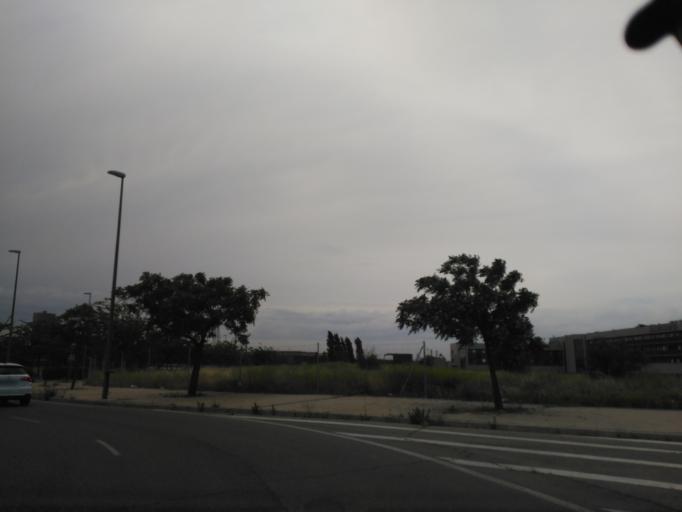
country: ES
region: Madrid
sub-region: Provincia de Madrid
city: Villaverde
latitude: 40.3343
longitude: -3.7202
